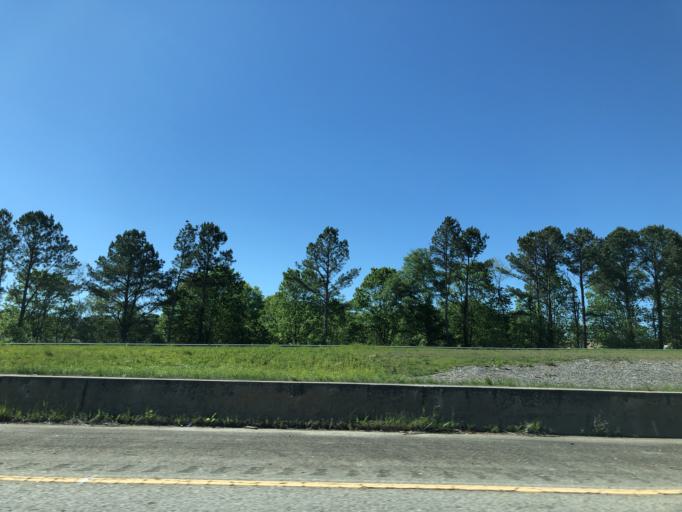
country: US
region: Georgia
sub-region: Oconee County
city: Bogart
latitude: 33.9384
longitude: -83.4639
